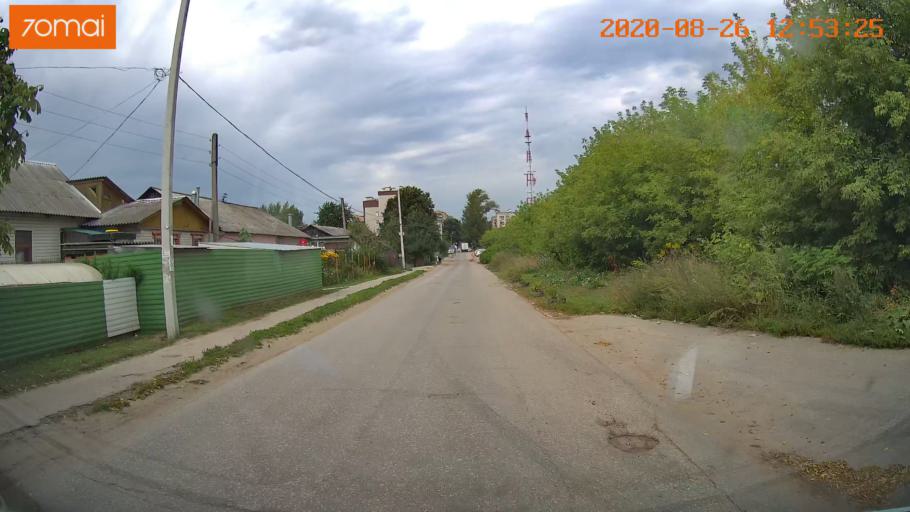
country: RU
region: Rjazan
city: Ryazan'
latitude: 54.6001
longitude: 39.7606
